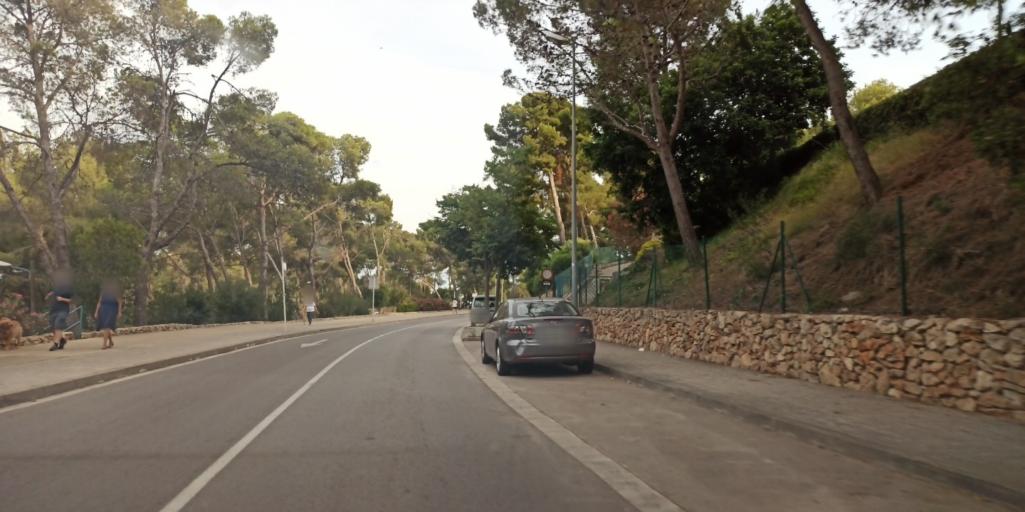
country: ES
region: Catalonia
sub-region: Provincia de Barcelona
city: Castelldefels
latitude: 41.2867
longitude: 1.9739
